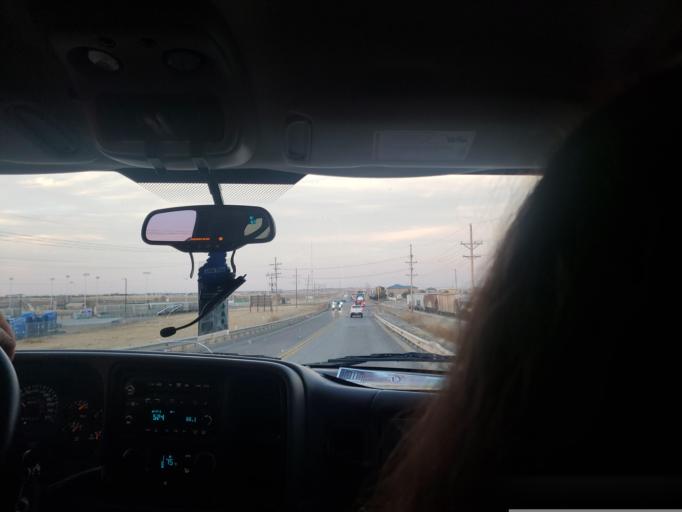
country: US
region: Kansas
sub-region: Seward County
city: Liberal
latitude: 37.0492
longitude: -100.9042
